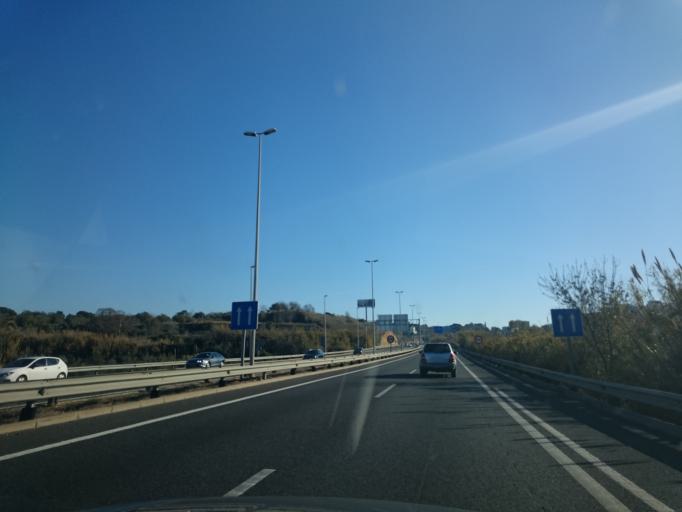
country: ES
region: Catalonia
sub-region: Provincia de Tarragona
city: Tarragona
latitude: 41.1284
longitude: 1.2333
